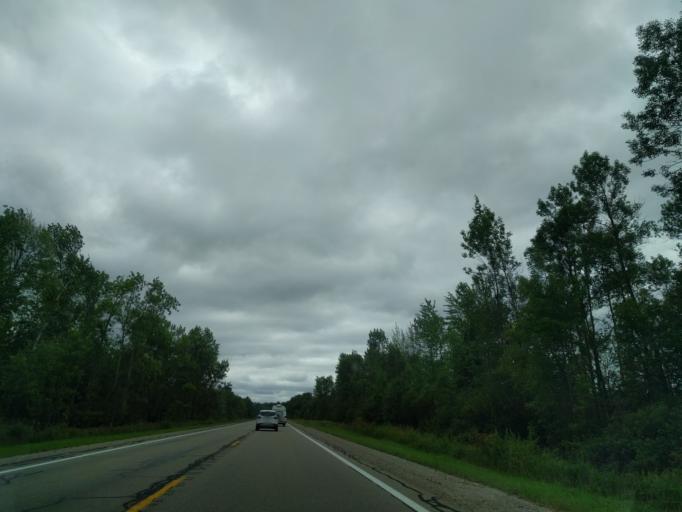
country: US
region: Michigan
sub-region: Menominee County
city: Menominee
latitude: 45.3272
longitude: -87.4258
